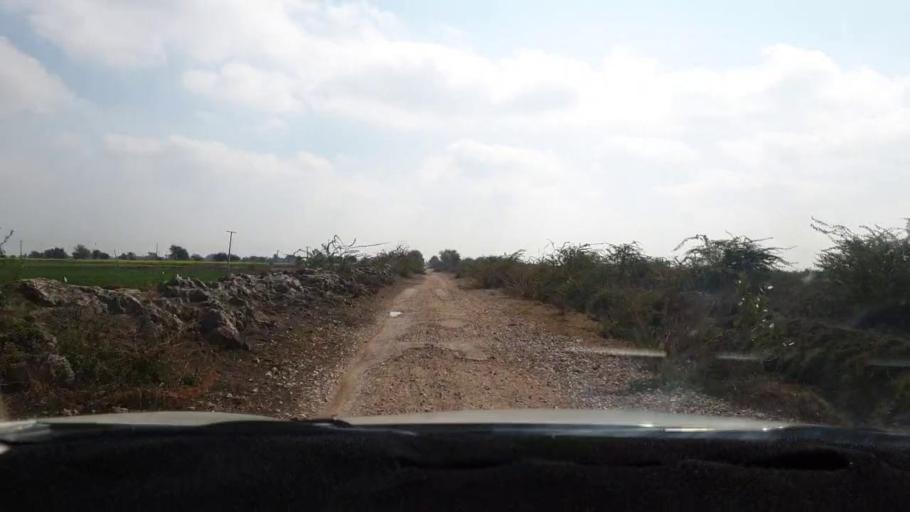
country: PK
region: Sindh
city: Berani
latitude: 25.7767
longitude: 68.9725
